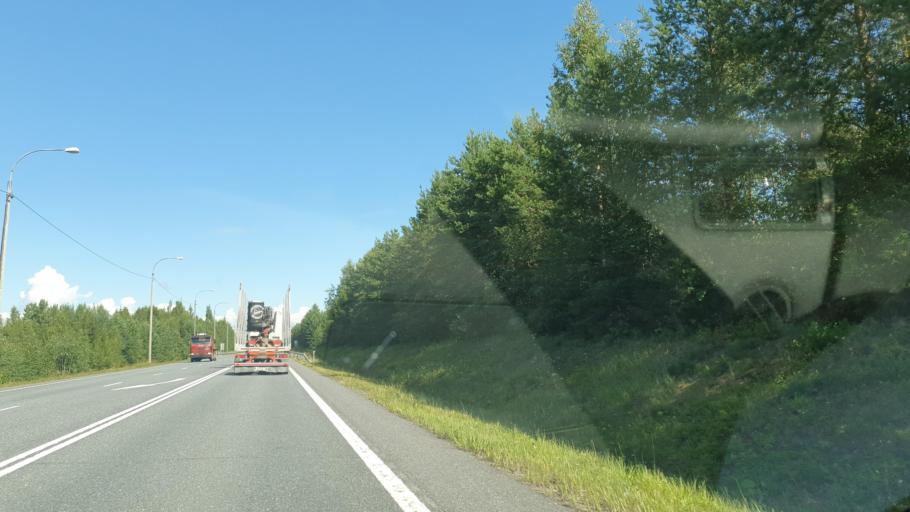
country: FI
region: Northern Savo
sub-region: Ylae-Savo
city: Iisalmi
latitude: 63.6143
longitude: 27.2207
